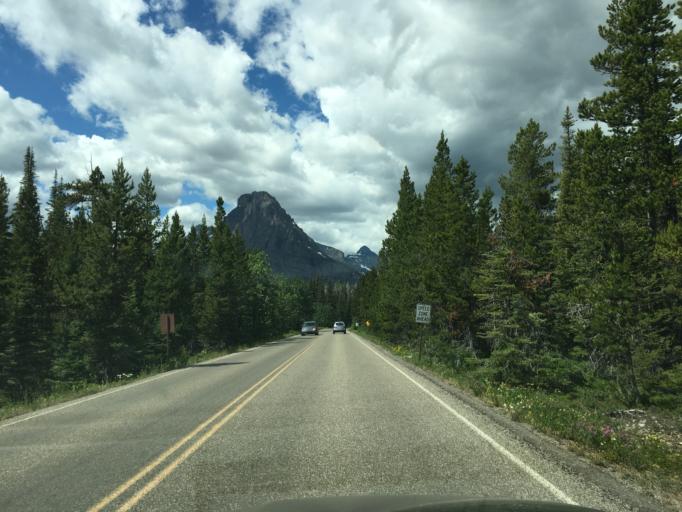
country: US
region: Montana
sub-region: Glacier County
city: South Browning
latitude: 48.4859
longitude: -113.3603
